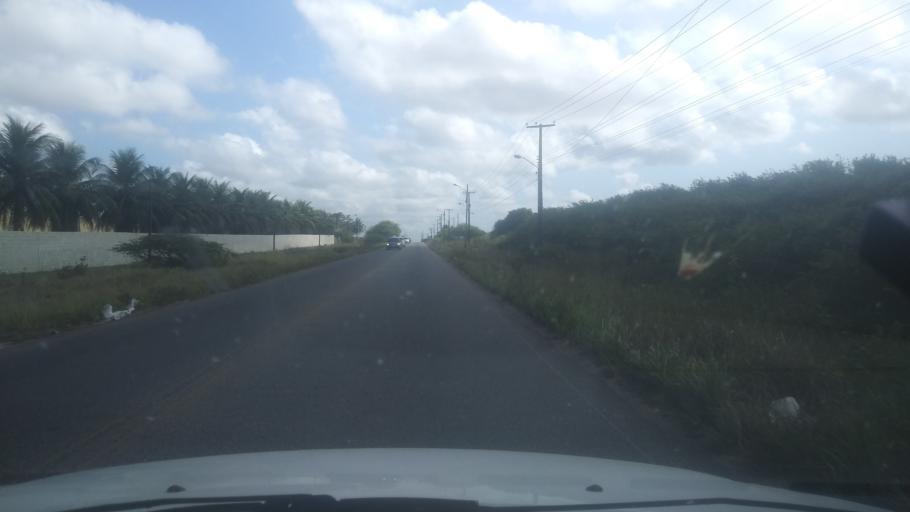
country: BR
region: Rio Grande do Norte
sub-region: Extremoz
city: Extremoz
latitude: -5.7176
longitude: -35.2774
